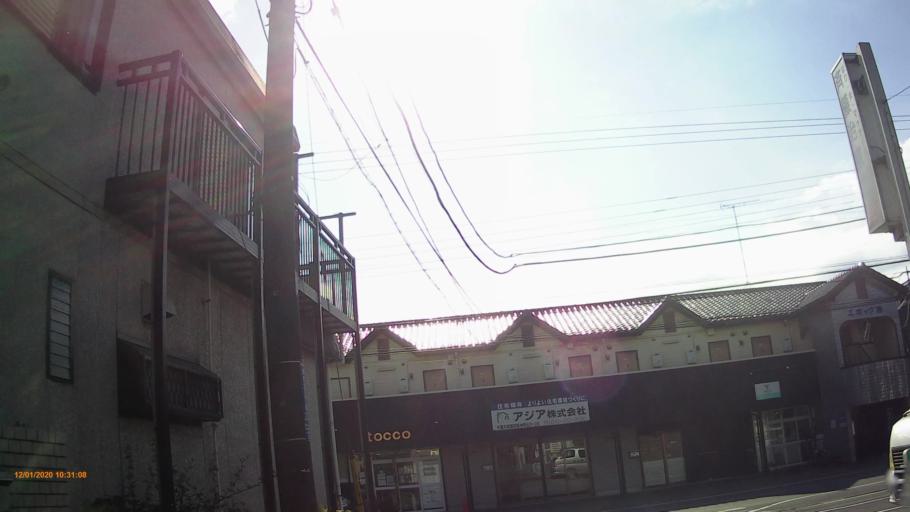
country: JP
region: Chiba
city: Yotsukaido
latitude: 35.6382
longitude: 140.1591
